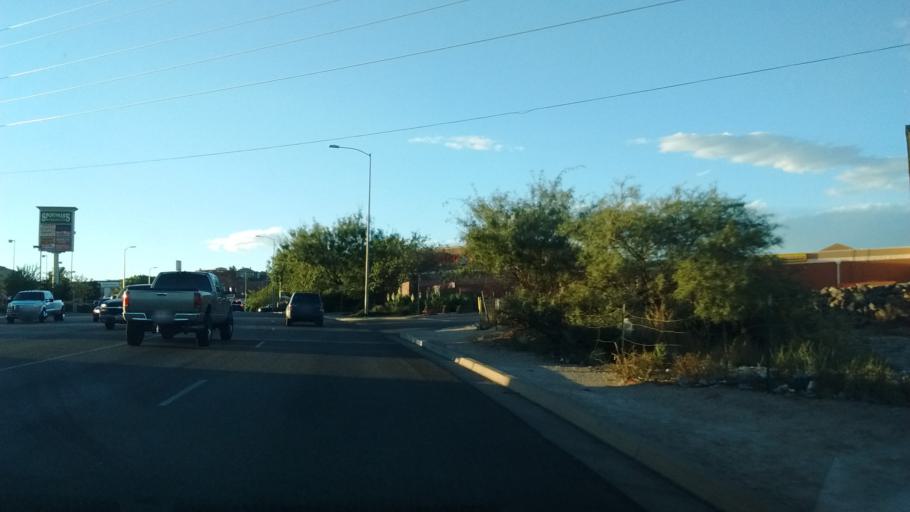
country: US
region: Utah
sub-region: Washington County
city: Washington
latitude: 37.1251
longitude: -113.5214
